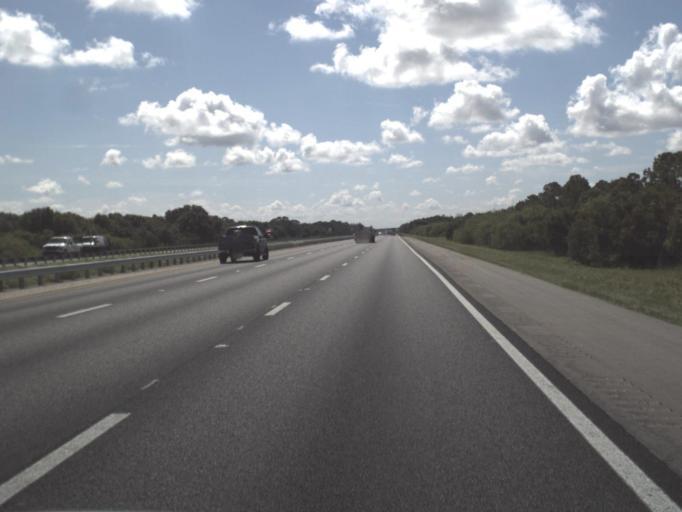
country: US
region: Florida
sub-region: Lee County
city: Suncoast Estates
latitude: 26.7515
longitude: -81.8644
